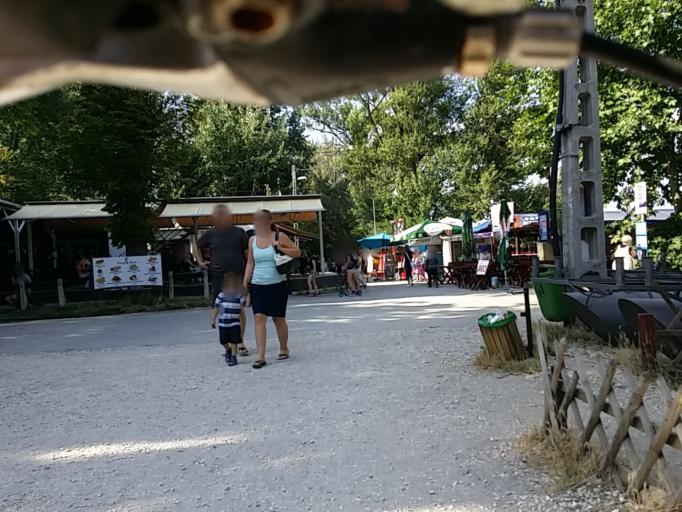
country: HU
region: Budapest
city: Budapest IV. keruelet
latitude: 47.5734
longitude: 19.0654
